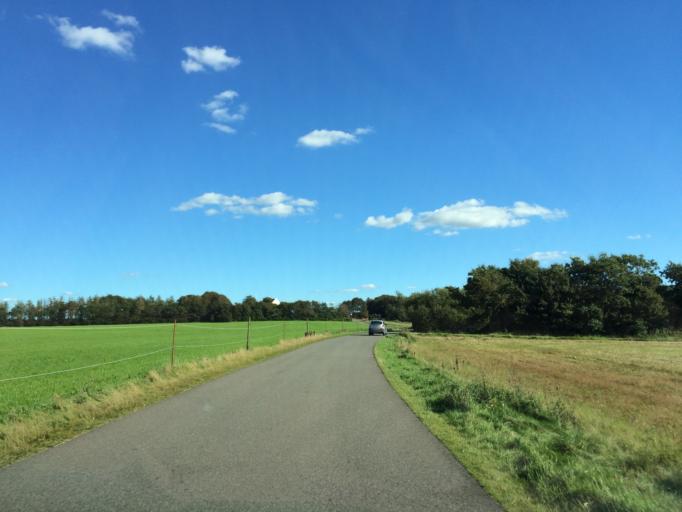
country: DK
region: Central Jutland
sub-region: Holstebro Kommune
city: Holstebro
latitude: 56.2636
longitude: 8.5399
